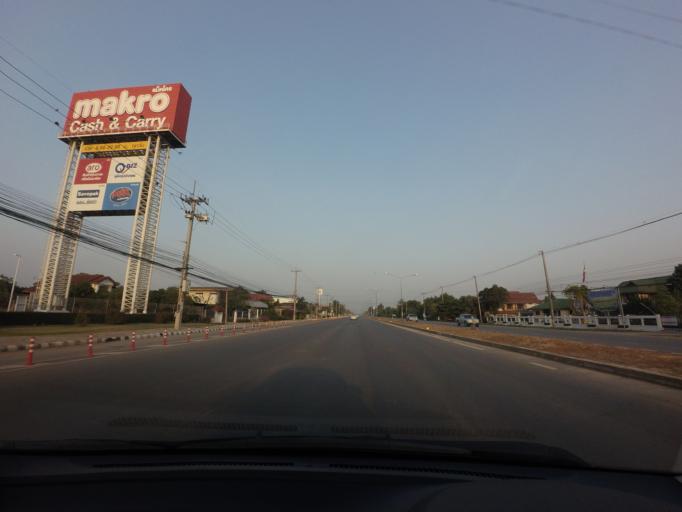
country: TH
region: Sukhothai
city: Sukhothai
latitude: 17.0149
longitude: 99.8465
